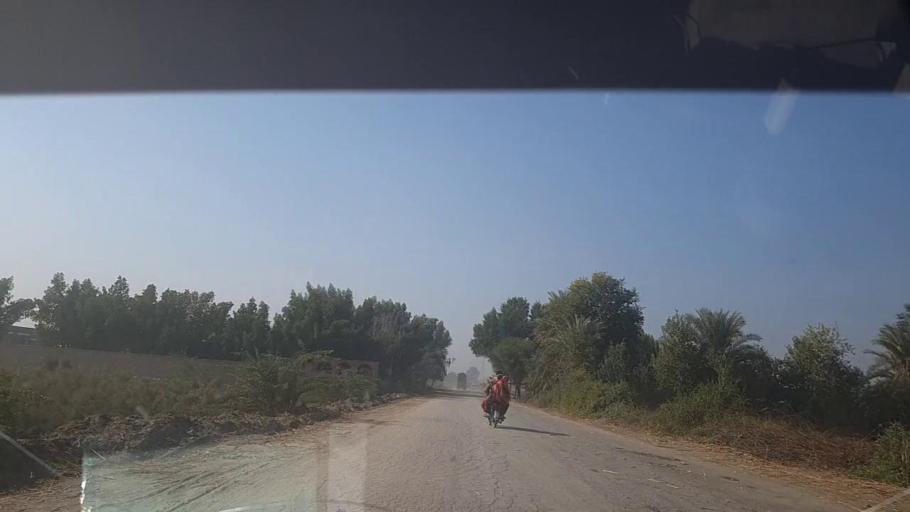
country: PK
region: Sindh
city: Kot Diji
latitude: 27.4356
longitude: 68.6432
